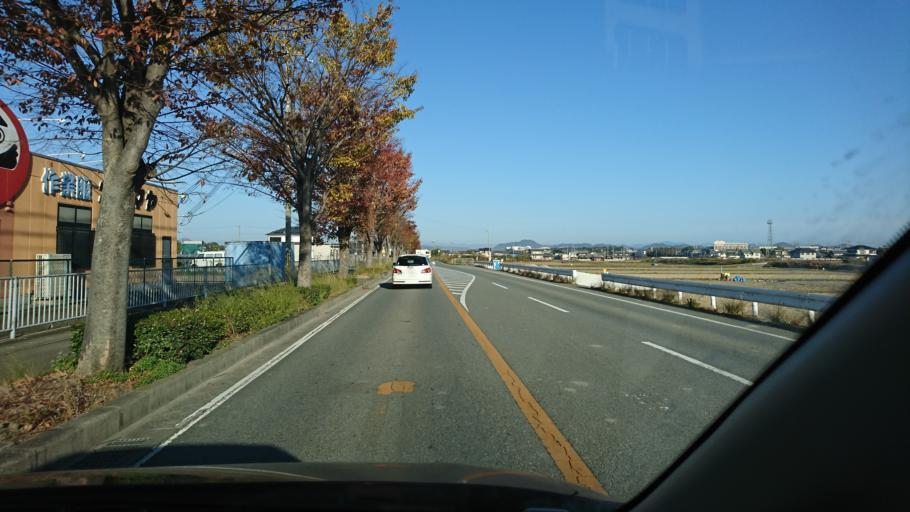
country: JP
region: Hyogo
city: Kakogawacho-honmachi
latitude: 34.7537
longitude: 134.8924
